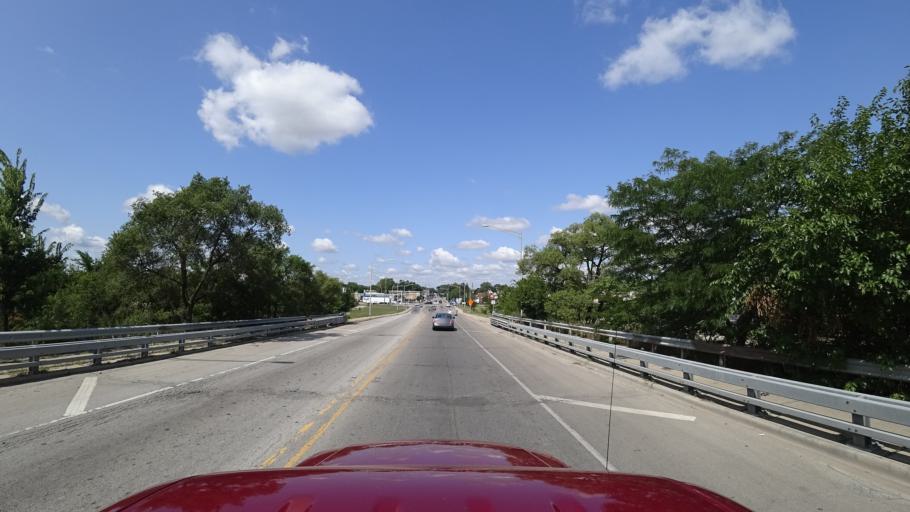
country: US
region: Illinois
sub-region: Cook County
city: Cicero
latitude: 41.8367
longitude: -87.7405
